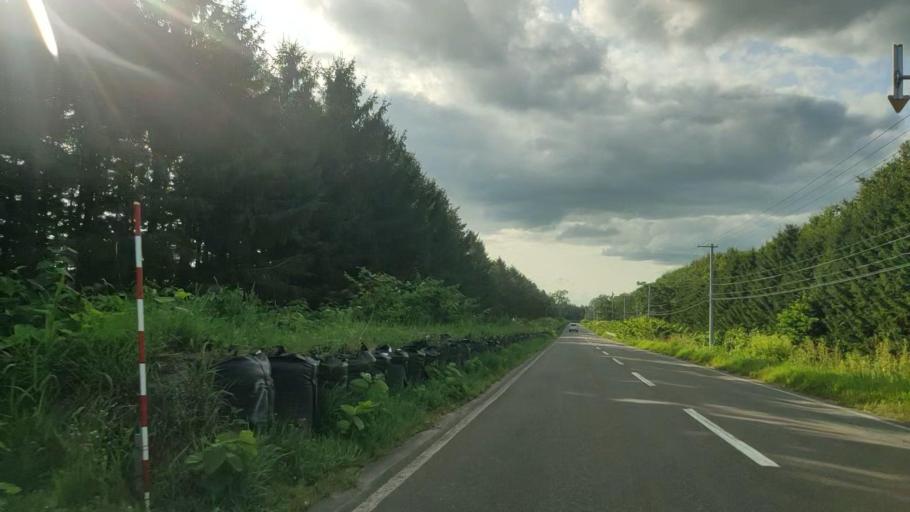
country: JP
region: Hokkaido
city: Makubetsu
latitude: 44.9024
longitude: 141.9087
